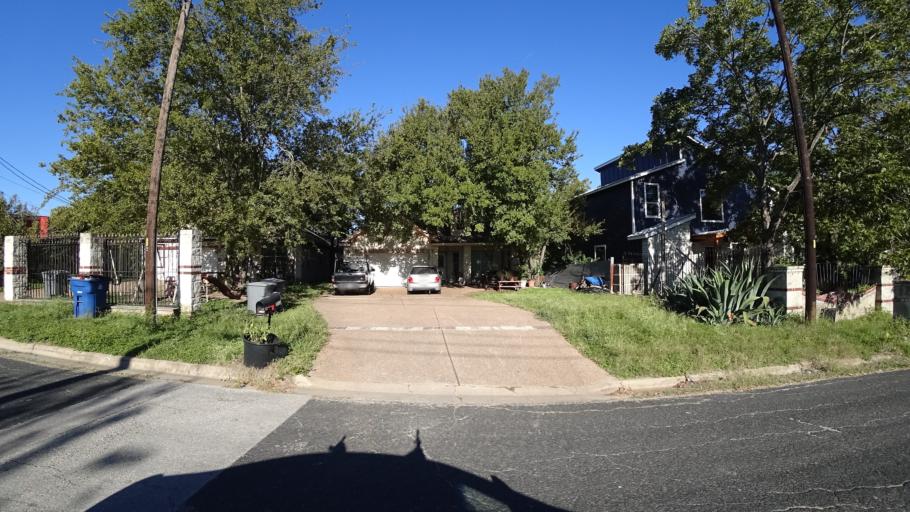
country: US
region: Texas
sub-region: Travis County
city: Austin
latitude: 30.2212
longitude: -97.6989
